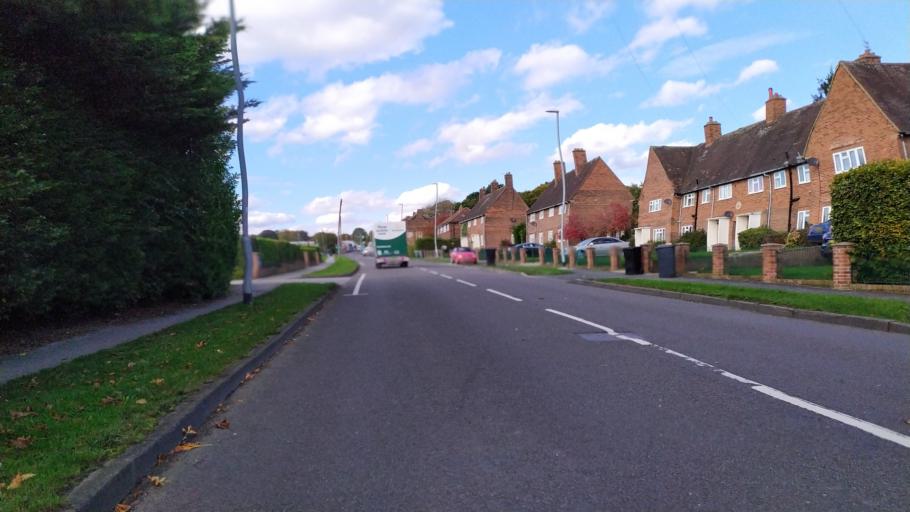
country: GB
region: England
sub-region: City and Borough of Leeds
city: Horsforth
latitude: 53.8204
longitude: -1.5947
